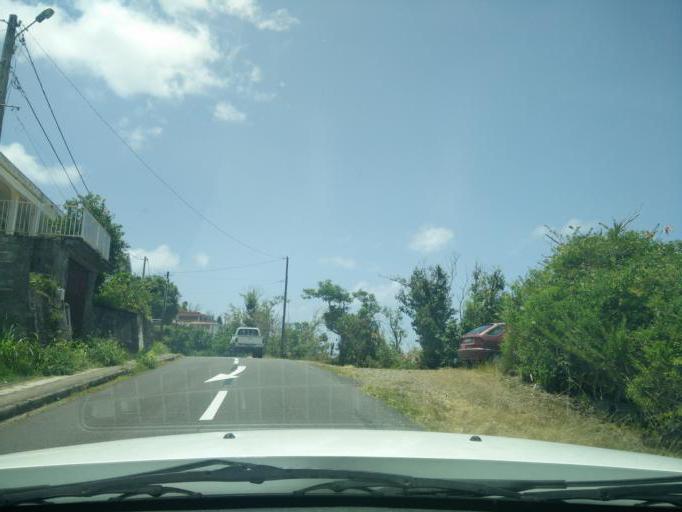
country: GP
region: Guadeloupe
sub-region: Guadeloupe
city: Gourbeyre
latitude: 15.9498
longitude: -61.7046
